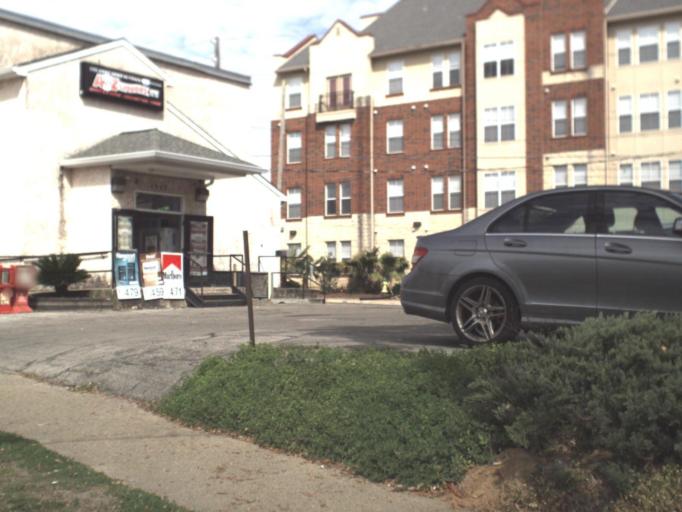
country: US
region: Florida
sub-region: Leon County
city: Tallahassee
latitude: 30.4487
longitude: -84.3034
